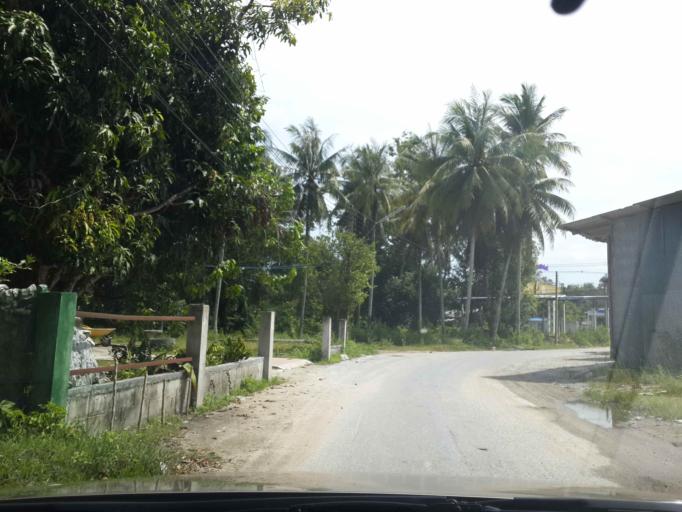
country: TH
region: Narathiwat
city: Rueso
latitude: 6.4047
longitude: 101.5177
